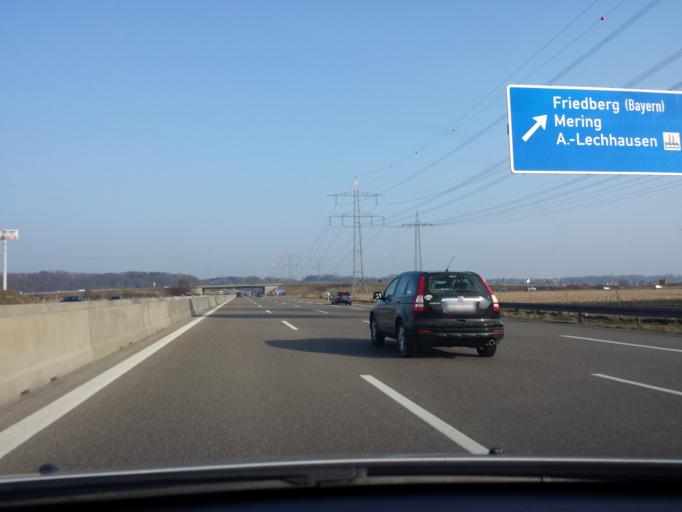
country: DE
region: Bavaria
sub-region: Swabia
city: Friedberg
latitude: 48.4051
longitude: 10.9486
